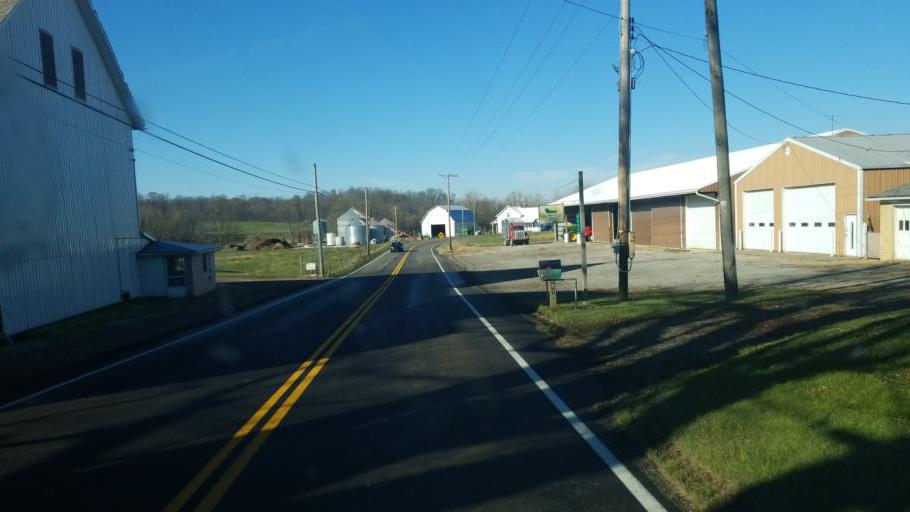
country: US
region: Ohio
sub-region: Holmes County
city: Millersburg
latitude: 40.6089
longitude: -81.8565
